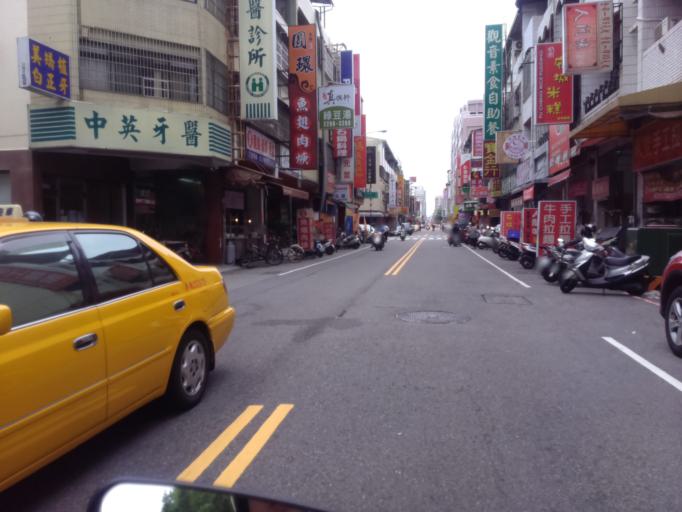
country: TW
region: Taiwan
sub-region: Taichung City
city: Taichung
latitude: 24.1714
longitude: 120.6766
